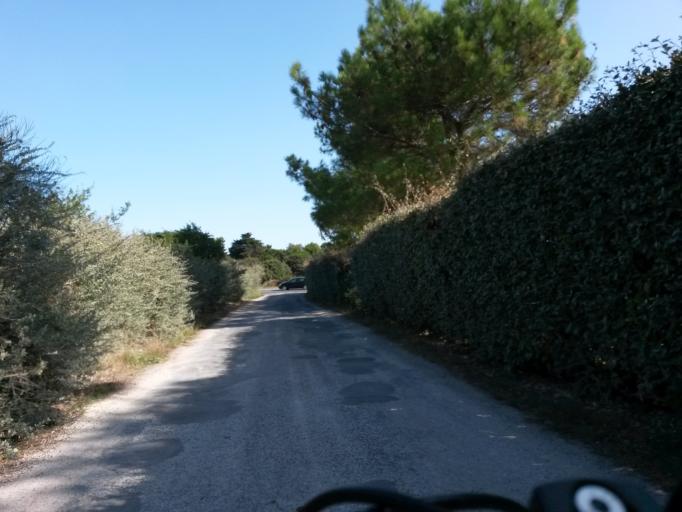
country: FR
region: Poitou-Charentes
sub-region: Departement de la Charente-Maritime
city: La Flotte
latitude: 46.1640
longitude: -1.3524
